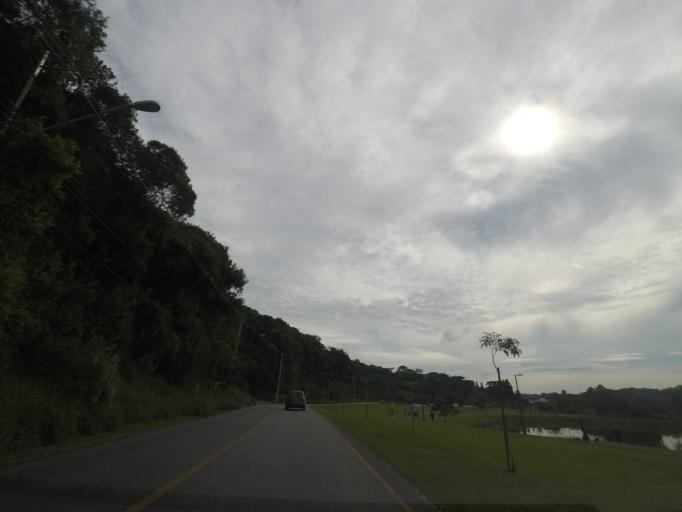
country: BR
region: Parana
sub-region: Curitiba
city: Curitiba
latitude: -25.3907
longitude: -49.3066
